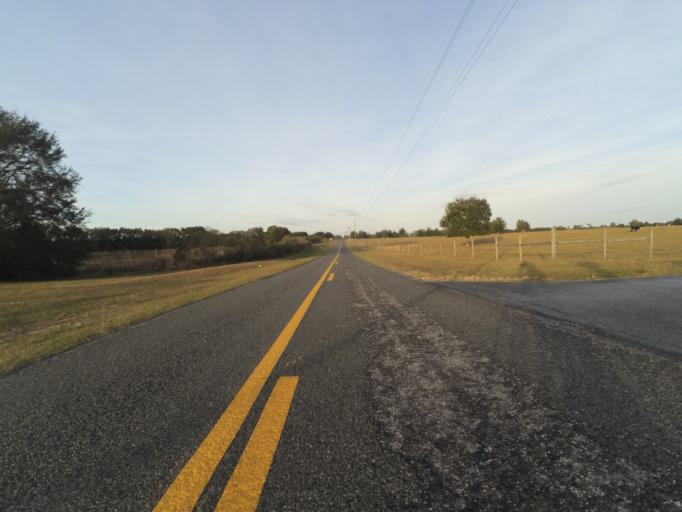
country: US
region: Florida
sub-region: Lake County
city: Umatilla
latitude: 28.9457
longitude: -81.6873
